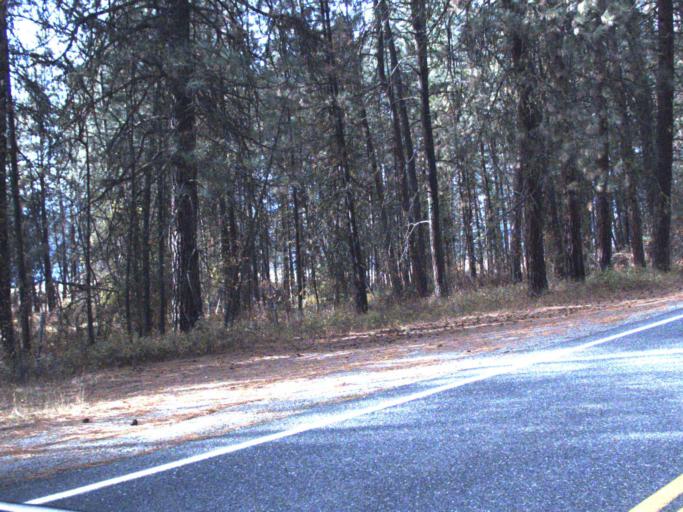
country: US
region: Washington
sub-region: Stevens County
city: Kettle Falls
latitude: 48.3014
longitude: -118.1482
